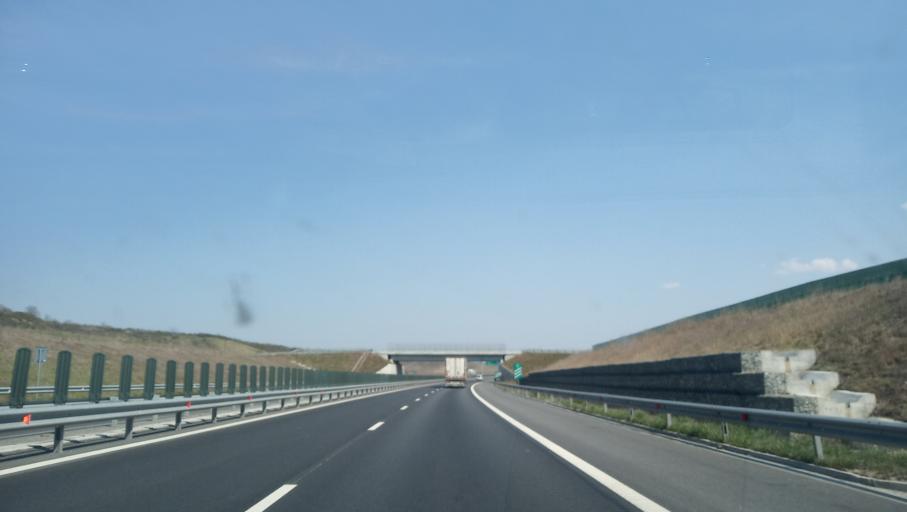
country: RO
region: Alba
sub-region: Comuna Miraslau
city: Miraslau
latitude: 46.3844
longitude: 23.7591
